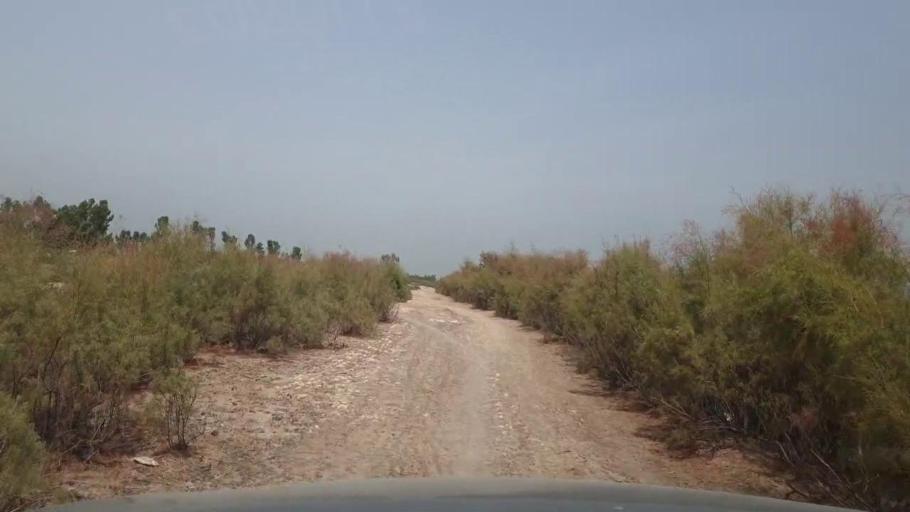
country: PK
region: Sindh
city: Garhi Yasin
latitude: 27.9207
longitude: 68.4140
